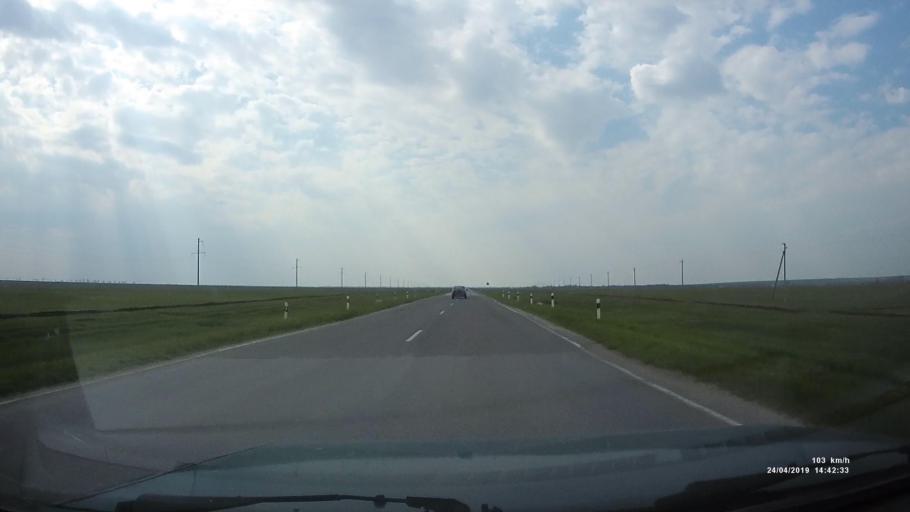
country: RU
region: Rostov
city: Remontnoye
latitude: 46.4526
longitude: 43.8595
